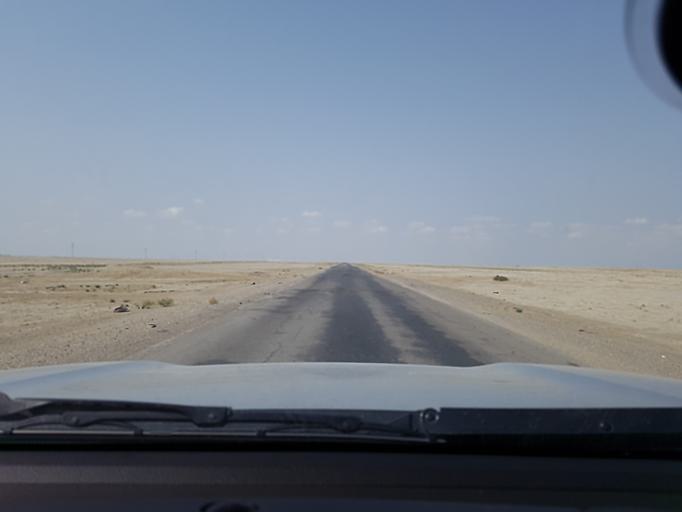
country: TM
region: Balkan
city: Gumdag
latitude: 38.6672
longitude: 54.4020
